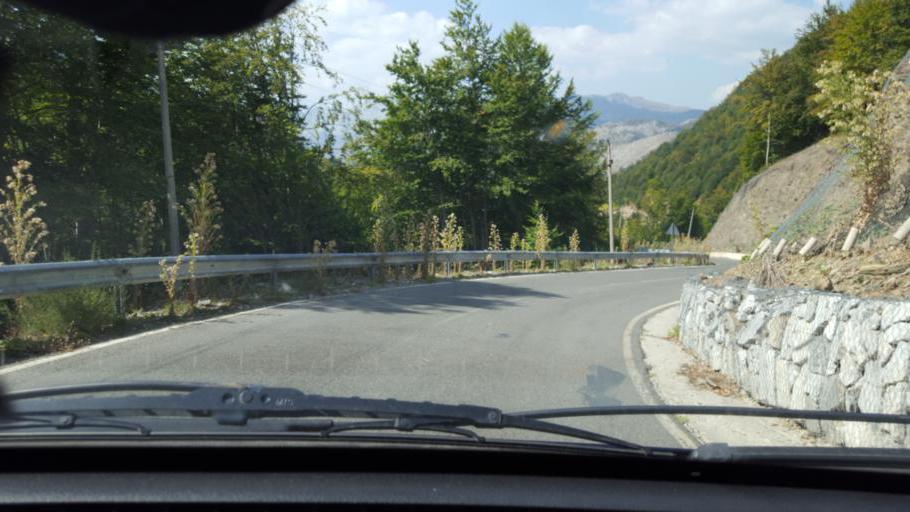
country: AL
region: Kukes
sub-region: Rrethi i Tropojes
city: Valbone
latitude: 42.5330
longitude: 19.7150
